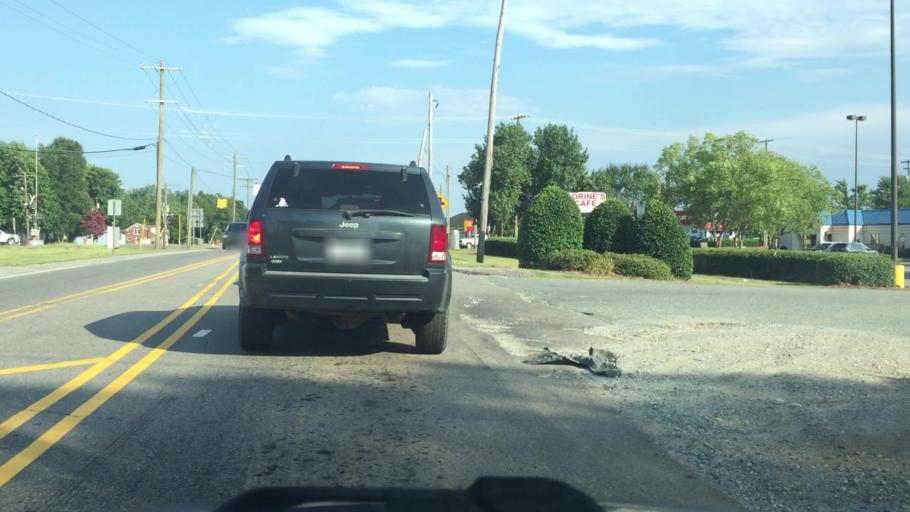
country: US
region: North Carolina
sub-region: Iredell County
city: Mooresville
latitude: 35.6013
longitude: -80.8123
